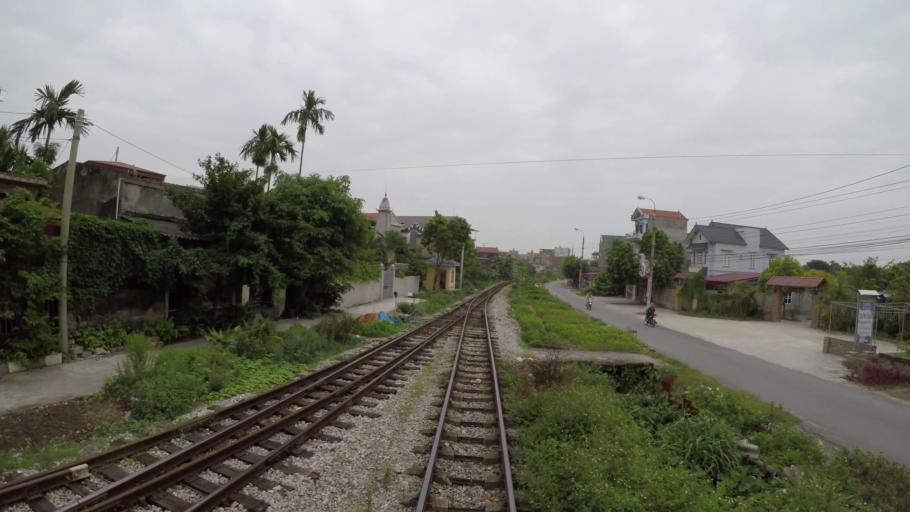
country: VN
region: Hai Duong
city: Phu Thai
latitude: 20.9684
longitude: 106.5017
